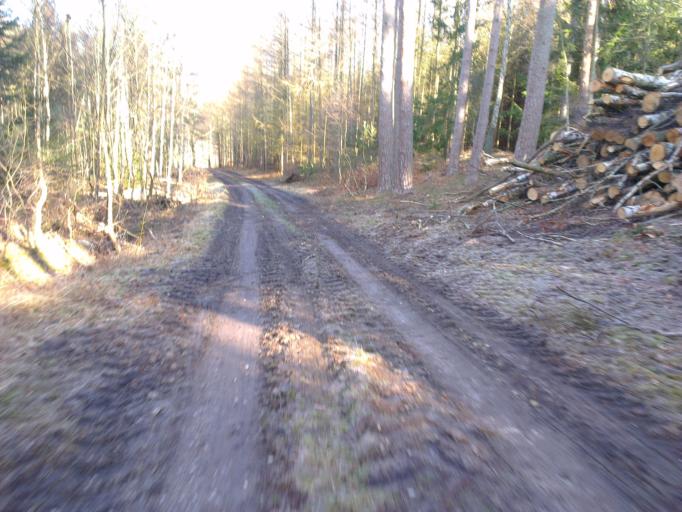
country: DK
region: Capital Region
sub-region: Frederikssund Kommune
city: Jaegerspris
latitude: 55.9042
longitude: 12.0137
